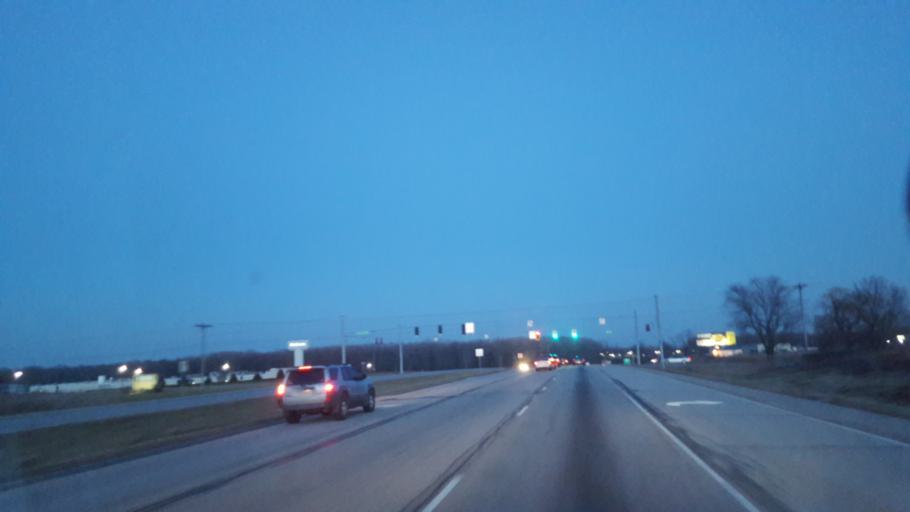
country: US
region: Indiana
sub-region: Kosciusko County
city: Warsaw
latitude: 41.2700
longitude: -85.8733
